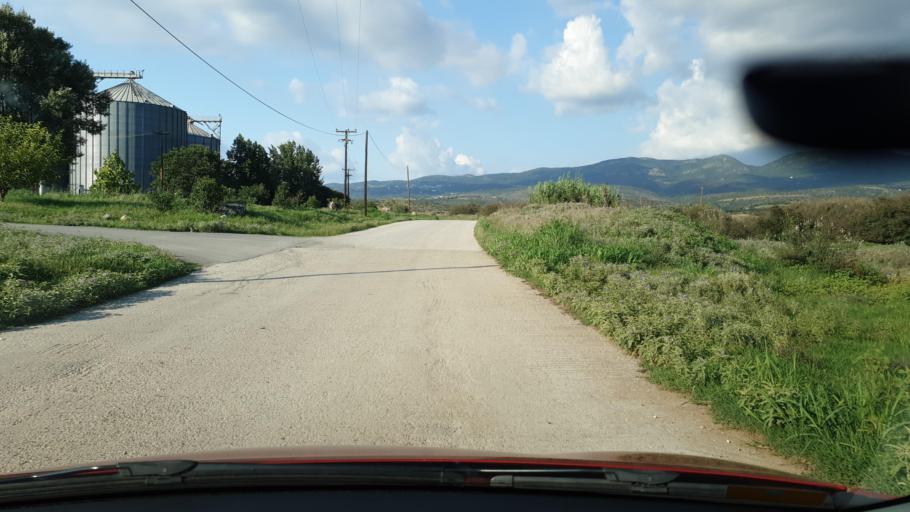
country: GR
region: Central Macedonia
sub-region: Nomos Thessalonikis
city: Vasilika
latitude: 40.4929
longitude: 23.1391
